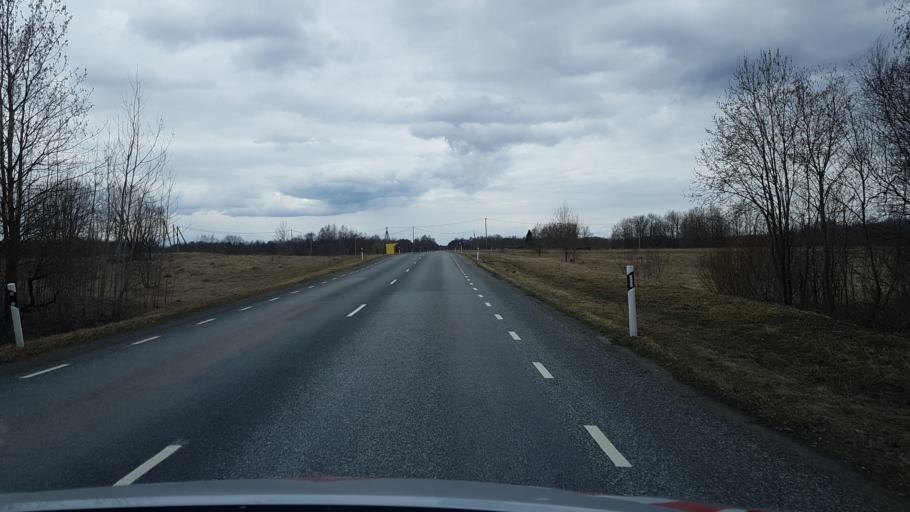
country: EE
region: Ida-Virumaa
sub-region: Narva-Joesuu linn
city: Narva-Joesuu
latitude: 59.3491
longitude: 28.0312
